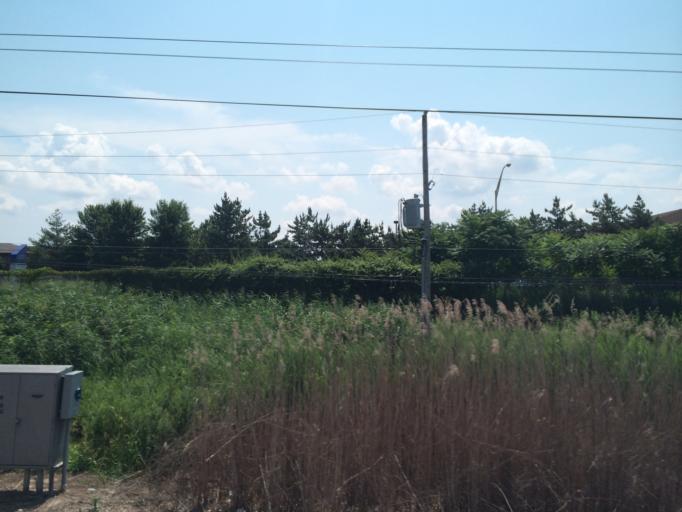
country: US
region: Pennsylvania
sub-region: Delaware County
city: Colwyn
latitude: 39.8862
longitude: -75.2498
